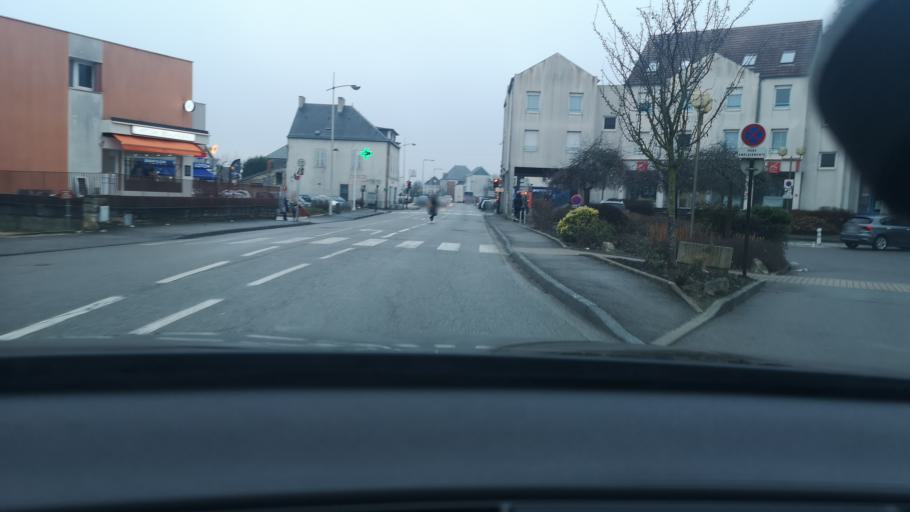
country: FR
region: Bourgogne
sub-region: Departement de la Cote-d'Or
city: Longvic
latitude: 47.2865
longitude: 5.0633
